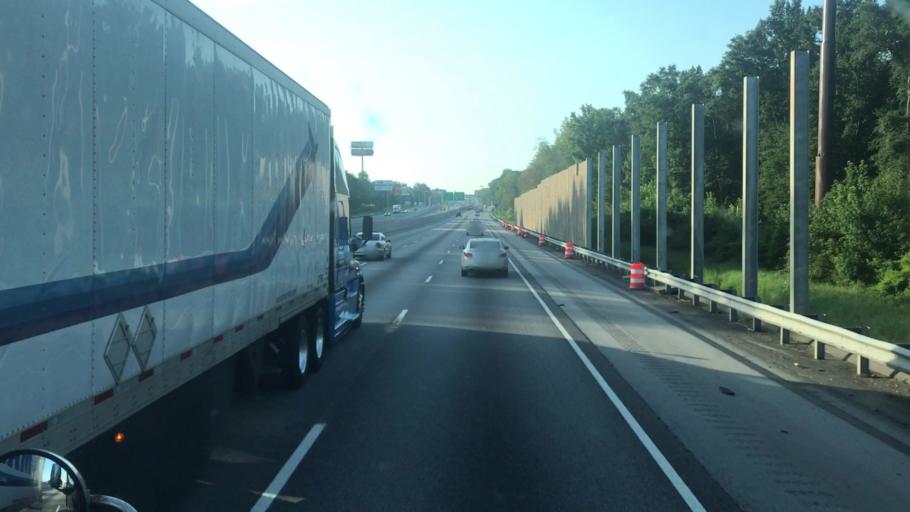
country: US
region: Georgia
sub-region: Henry County
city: McDonough
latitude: 33.4476
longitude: -84.2003
